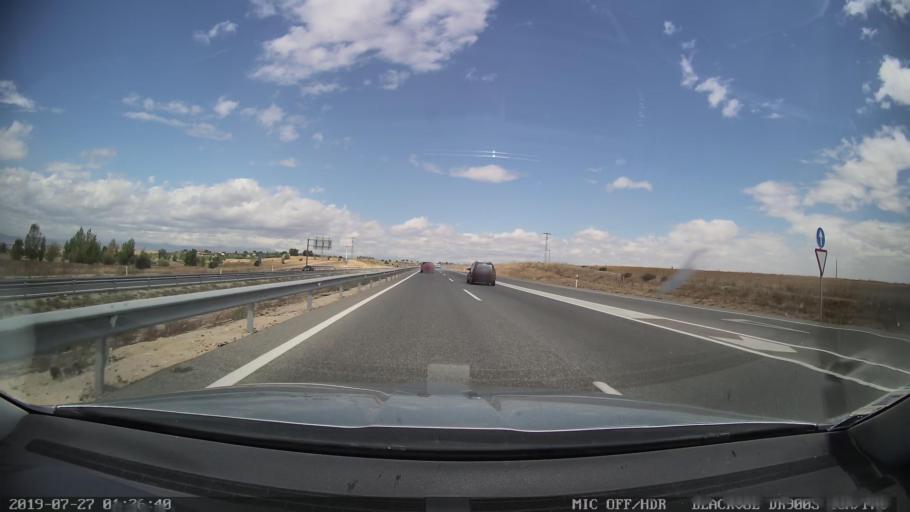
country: ES
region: Castille-La Mancha
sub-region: Province of Toledo
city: La Torre de Esteban Hambran
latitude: 40.1607
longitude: -4.1705
